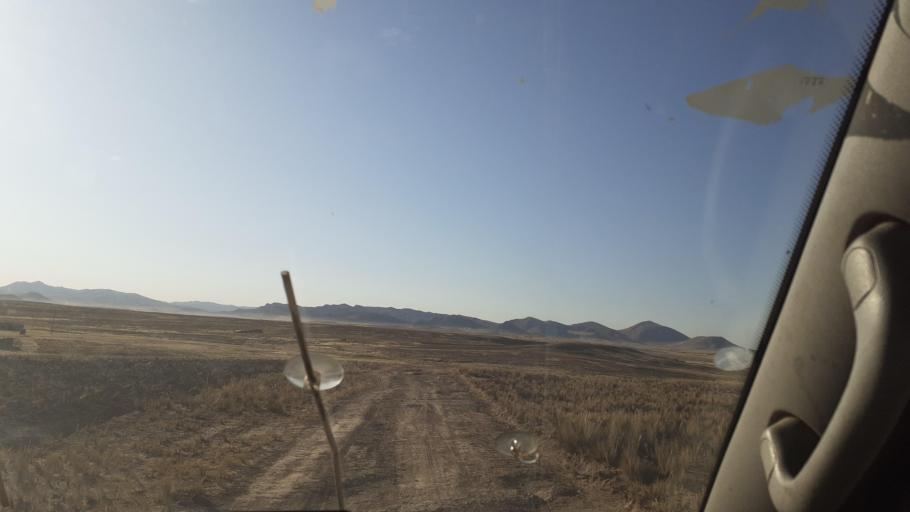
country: BO
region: La Paz
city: Tiahuanaco
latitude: -16.9957
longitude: -68.7275
